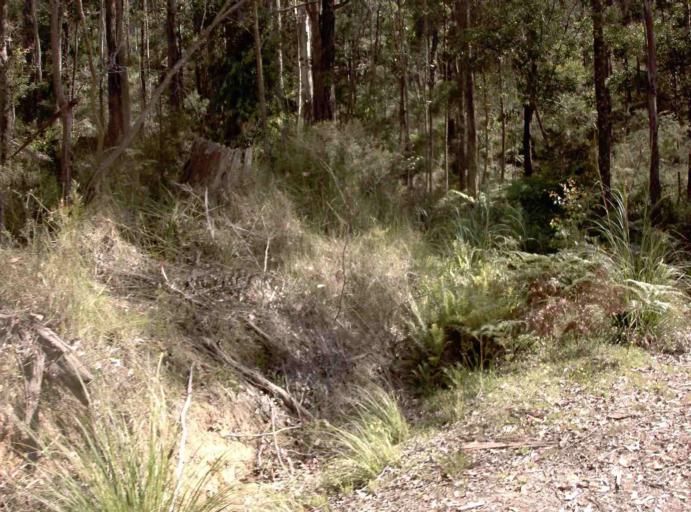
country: AU
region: New South Wales
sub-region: Bombala
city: Bombala
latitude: -37.3782
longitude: 148.6344
